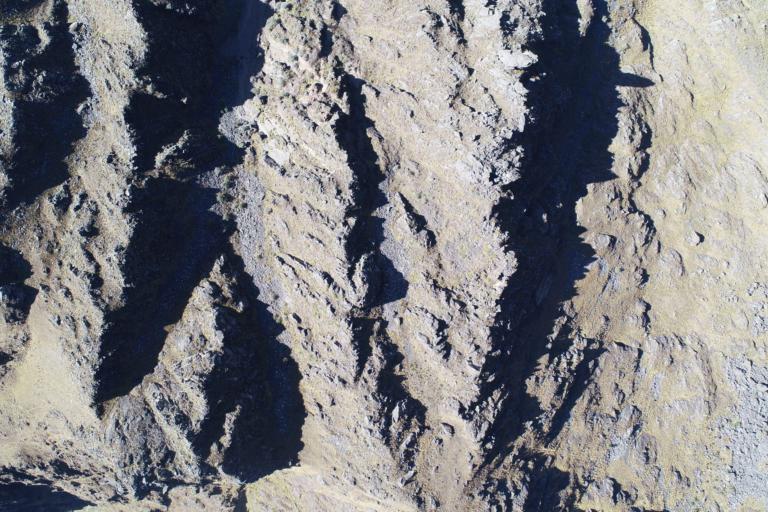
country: BO
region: La Paz
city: Sorata
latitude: -15.6558
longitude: -68.5328
